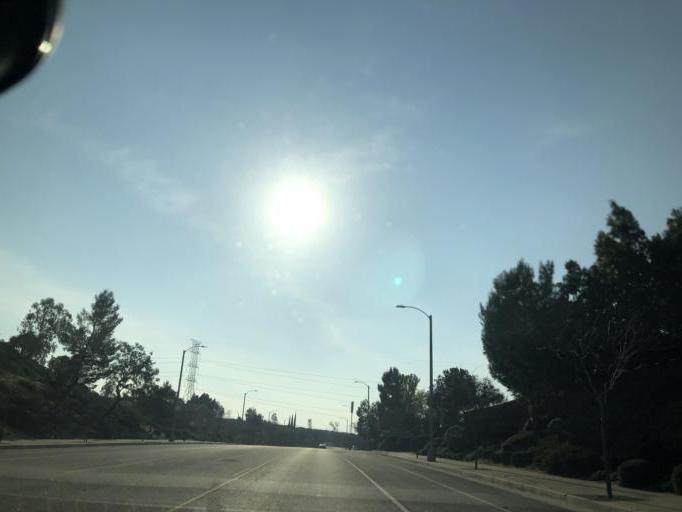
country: US
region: California
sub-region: Los Angeles County
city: San Fernando
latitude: 34.2945
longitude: -118.4645
